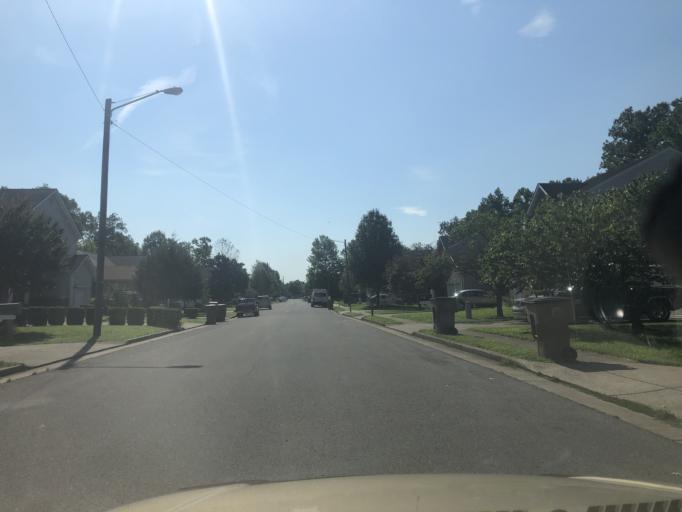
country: US
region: Tennessee
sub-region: Davidson County
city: Lakewood
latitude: 36.2392
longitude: -86.6968
